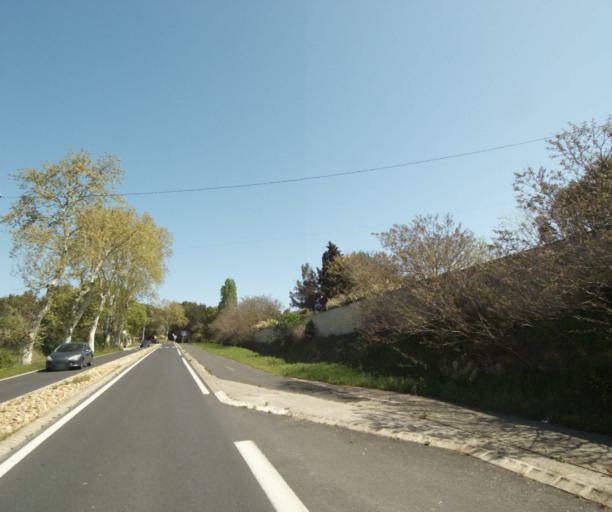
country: FR
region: Languedoc-Roussillon
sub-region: Departement de l'Herault
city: Castelnau-le-Lez
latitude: 43.6467
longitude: 3.8991
